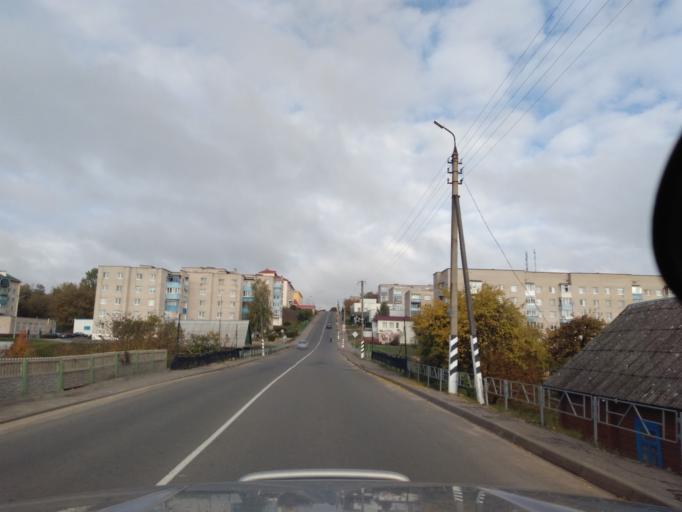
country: BY
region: Minsk
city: Kapyl'
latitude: 53.1484
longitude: 27.0945
